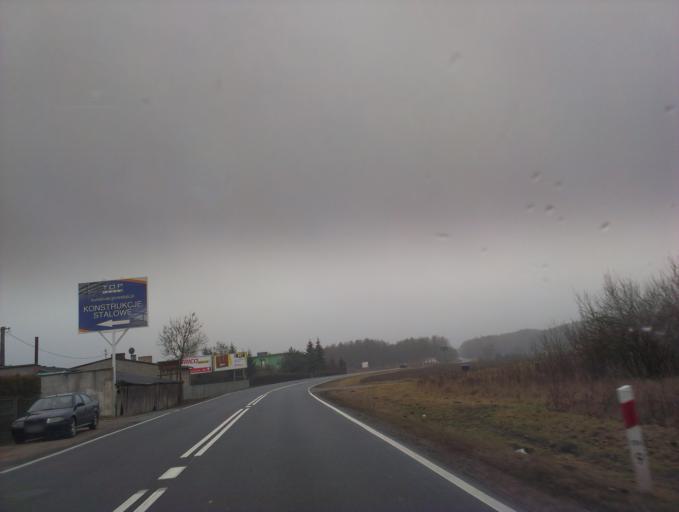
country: PL
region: Greater Poland Voivodeship
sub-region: Powiat pilski
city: Pila
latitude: 53.2160
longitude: 16.7860
